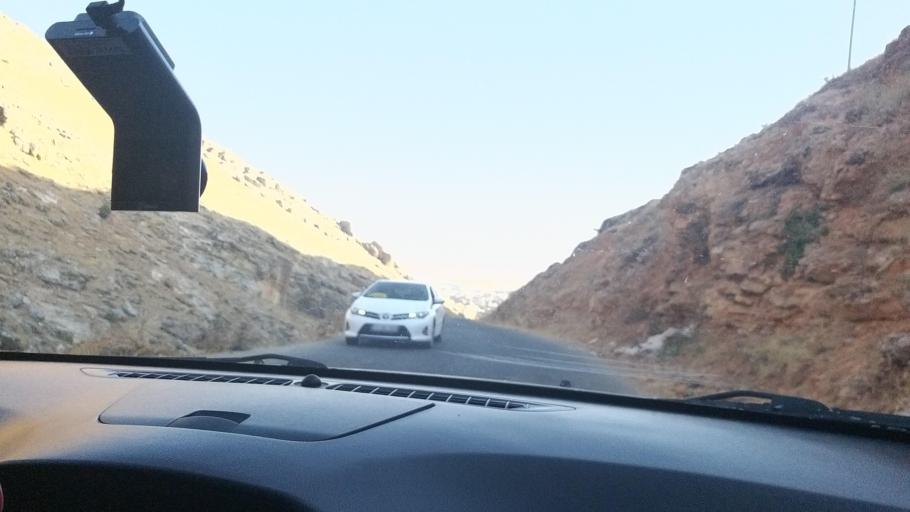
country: TR
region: Diyarbakir
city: Silvan
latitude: 38.1605
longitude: 41.0028
